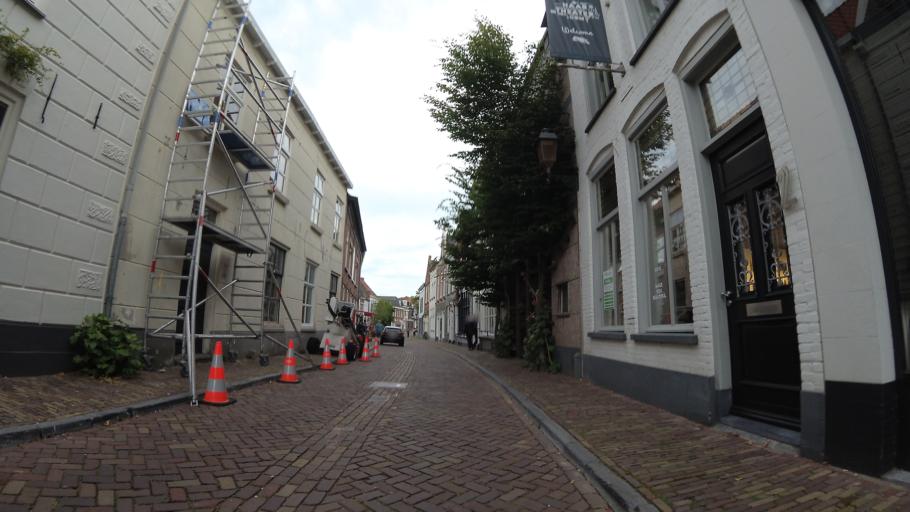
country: NL
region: North Brabant
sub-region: Gemeente Geertruidenberg
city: Geertruidenberg
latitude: 51.7002
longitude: 4.8624
